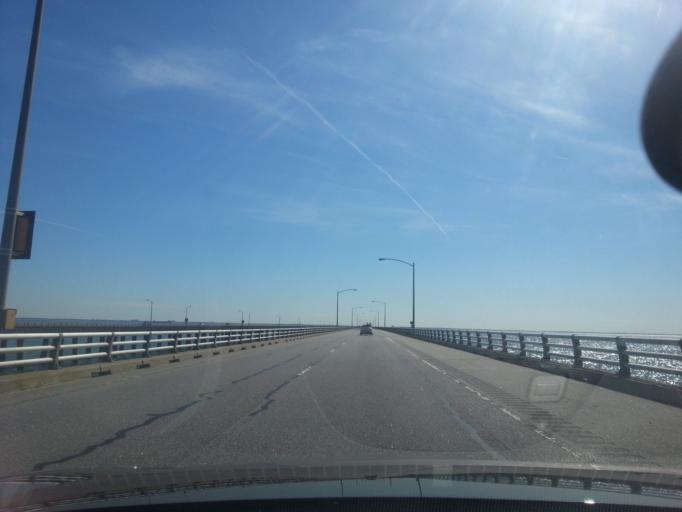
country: US
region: Virginia
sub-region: City of Virginia Beach
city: Virginia Beach
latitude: 37.0229
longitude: -76.0902
